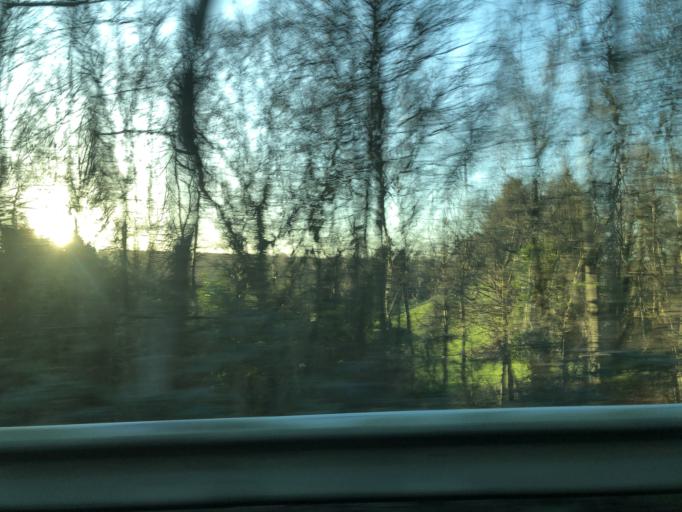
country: GB
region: England
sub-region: Surrey
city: Godstone
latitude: 51.2422
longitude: -0.0476
